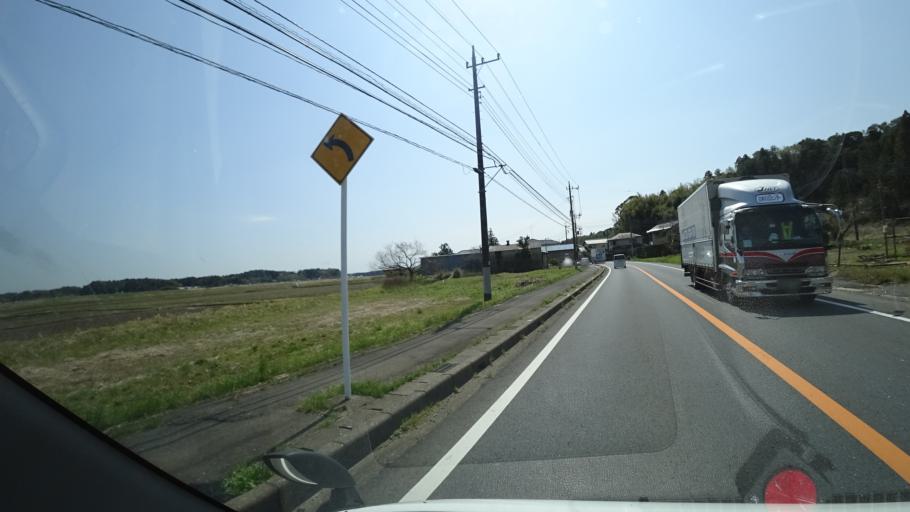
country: JP
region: Chiba
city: Narita
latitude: 35.8170
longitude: 140.3056
